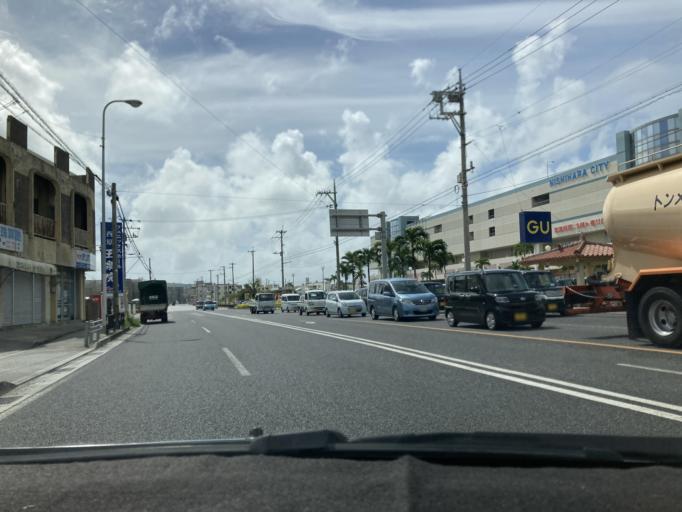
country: JP
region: Okinawa
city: Ginowan
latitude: 26.2251
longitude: 127.7661
